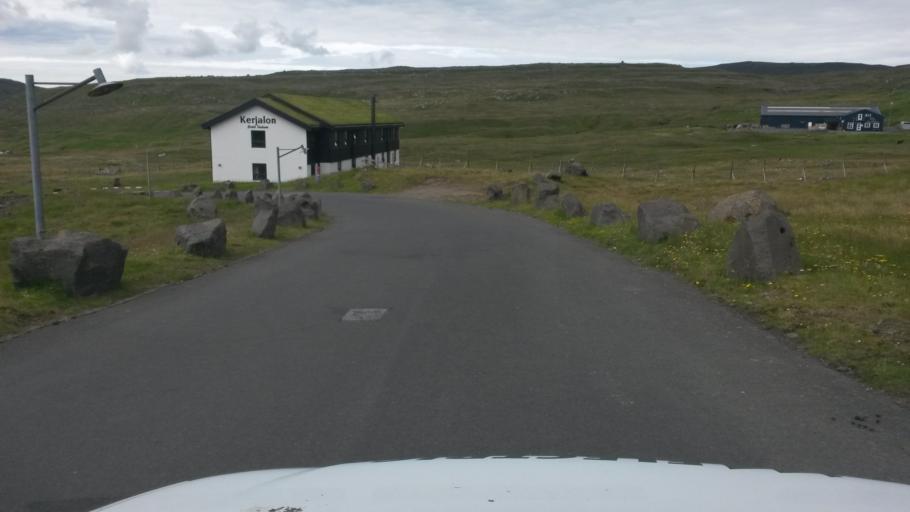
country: FO
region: Streymoy
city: Hoyvik
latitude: 62.0131
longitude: -6.8009
